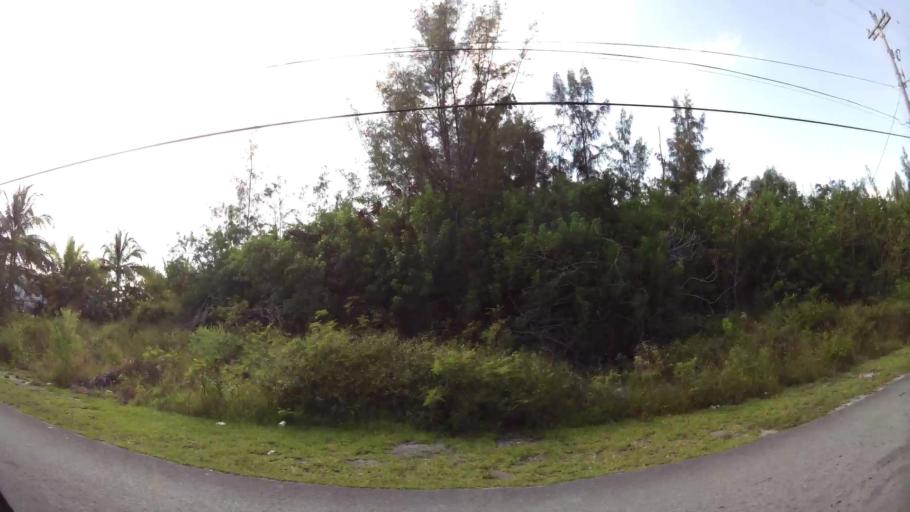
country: BS
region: Freeport
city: Lucaya
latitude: 26.5060
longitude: -78.6584
